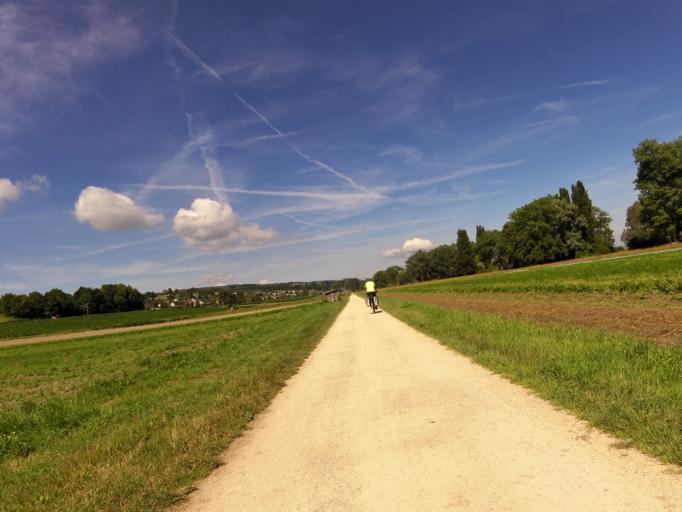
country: CH
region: Thurgau
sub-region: Kreuzlingen District
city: Gottlieben
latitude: 47.6627
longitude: 9.1243
